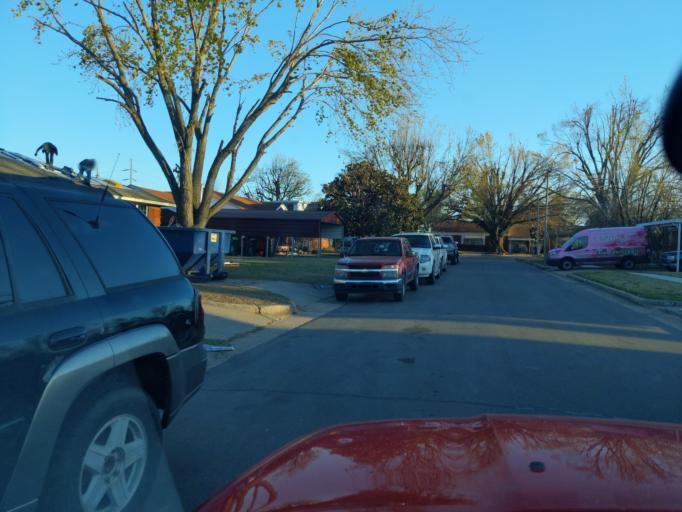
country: US
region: Oklahoma
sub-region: Oklahoma County
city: Oklahoma City
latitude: 35.4146
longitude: -97.5225
